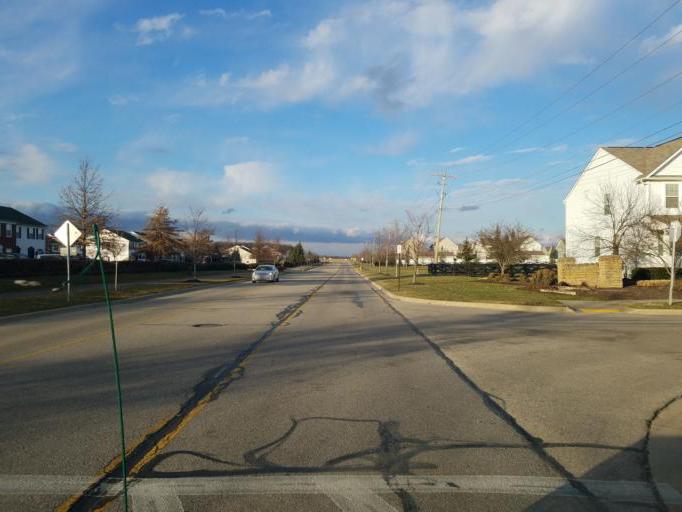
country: US
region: Ohio
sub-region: Delaware County
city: Delaware
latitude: 40.3178
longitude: -83.1087
